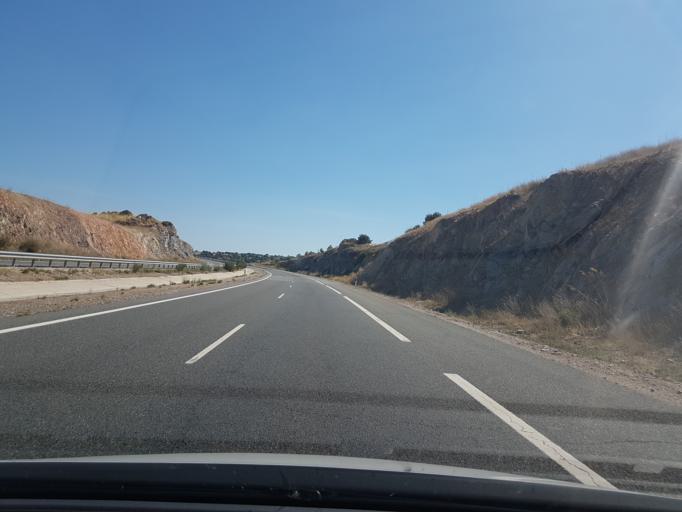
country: ES
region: Castille and Leon
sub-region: Provincia de Avila
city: Cardenosa
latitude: 40.7396
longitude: -4.7574
